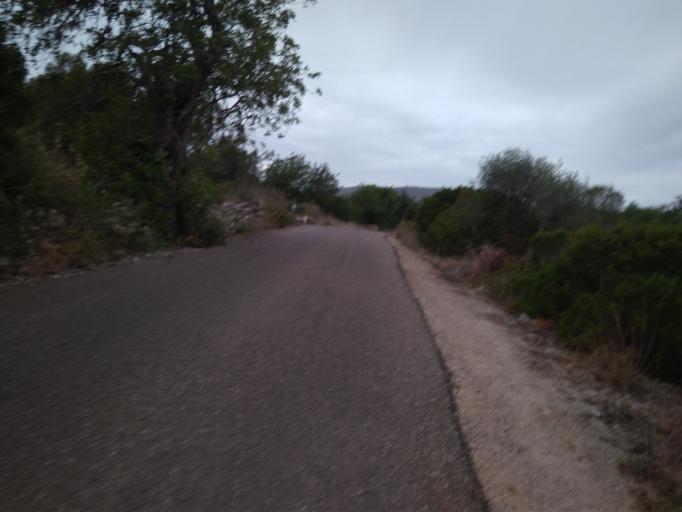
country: PT
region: Faro
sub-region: Faro
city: Santa Barbara de Nexe
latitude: 37.1033
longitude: -7.9540
